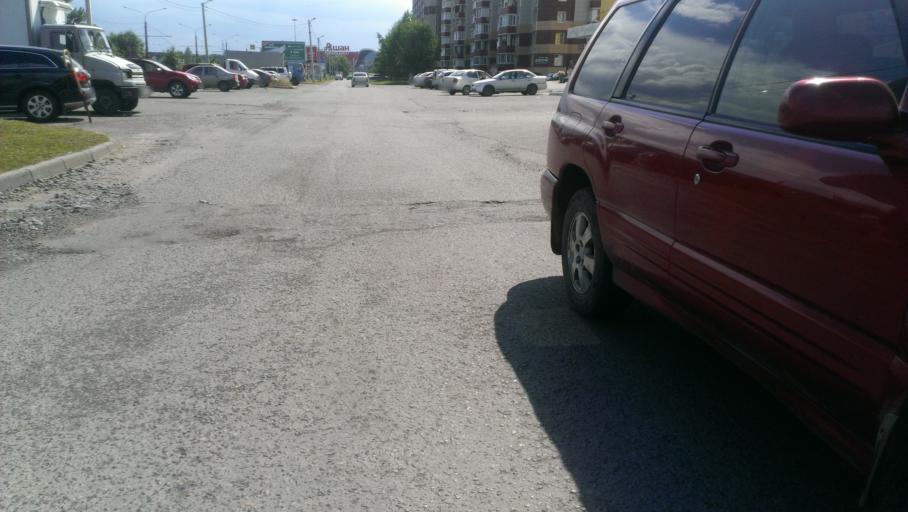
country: RU
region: Altai Krai
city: Novosilikatnyy
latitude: 53.3321
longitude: 83.6925
